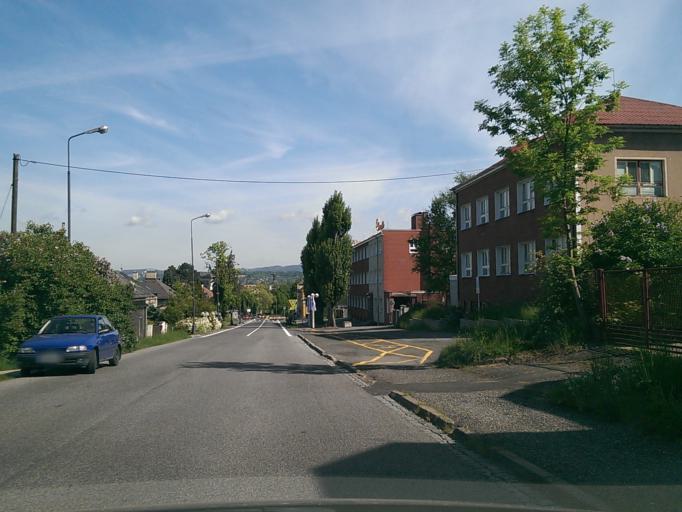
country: CZ
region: Liberecky
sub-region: Okres Semily
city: Turnov
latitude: 50.5808
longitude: 15.1574
